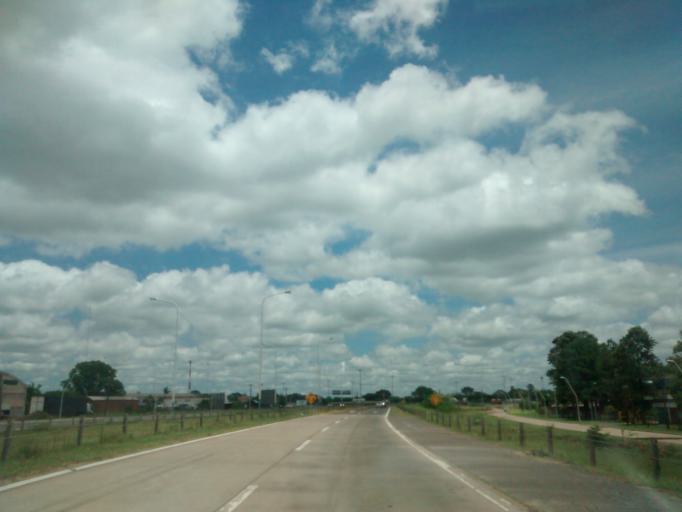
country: AR
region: Chaco
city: Fontana
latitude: -27.4125
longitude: -58.9978
